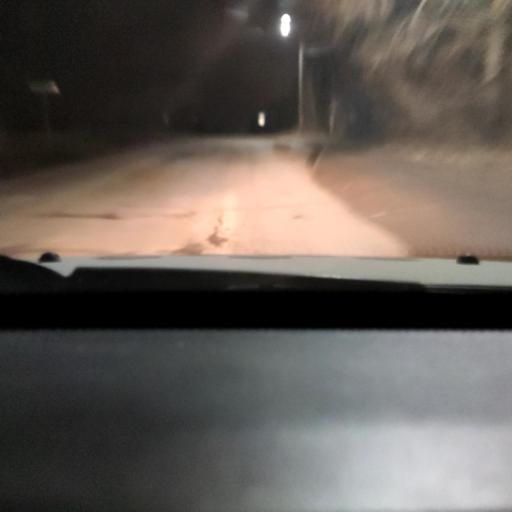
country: RU
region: Perm
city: Gamovo
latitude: 57.8749
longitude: 56.1019
